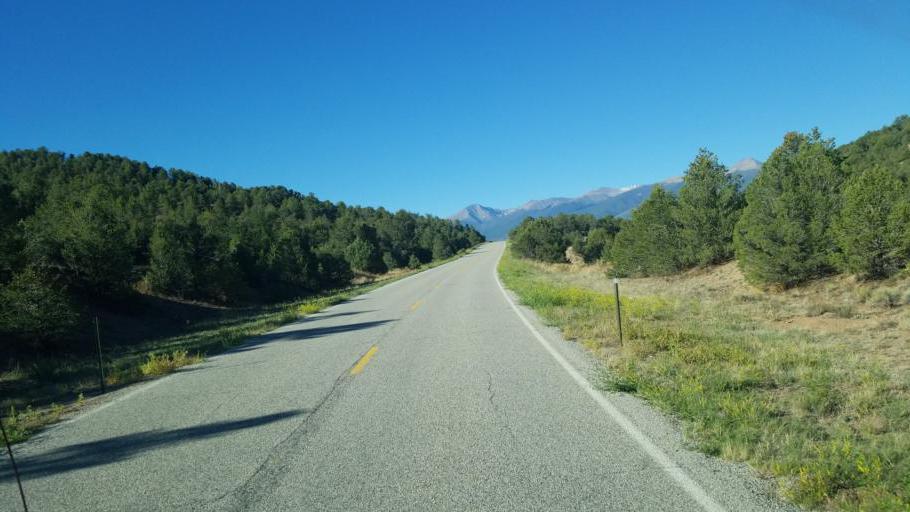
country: US
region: Colorado
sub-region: Custer County
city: Westcliffe
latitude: 38.3682
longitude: -105.5857
